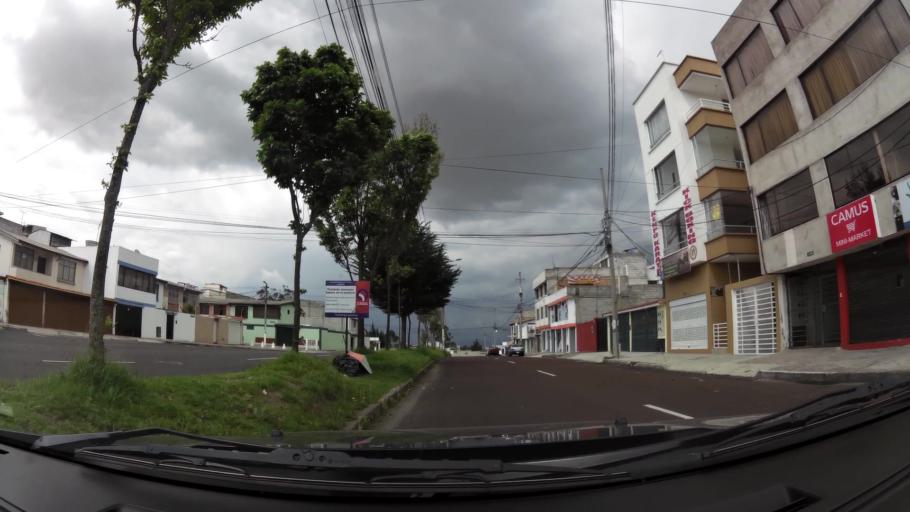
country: EC
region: Pichincha
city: Quito
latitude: -0.0915
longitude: -78.4685
